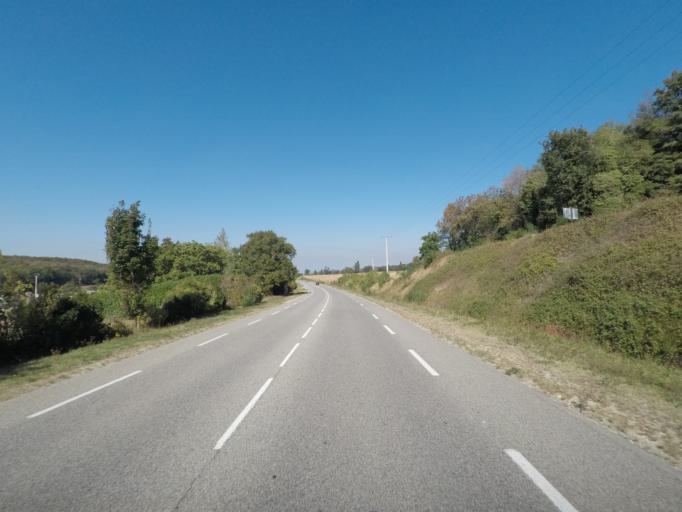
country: FR
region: Rhone-Alpes
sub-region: Departement de la Drome
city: Eurre
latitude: 44.7904
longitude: 5.0227
